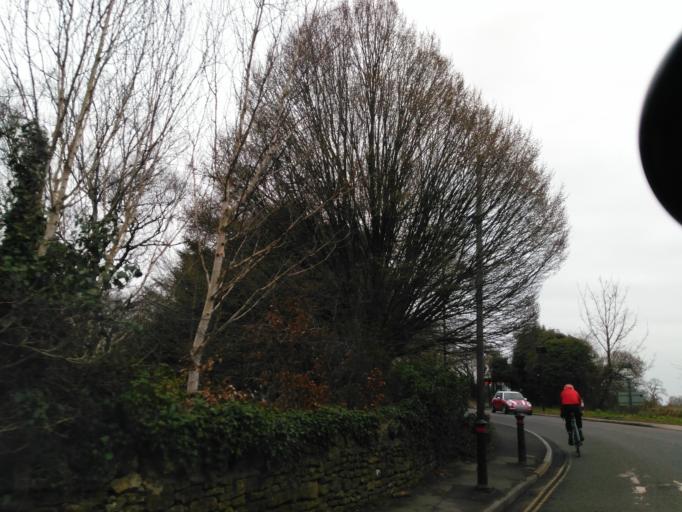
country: GB
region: England
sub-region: Bath and North East Somerset
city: Bath
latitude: 51.3747
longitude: -2.3294
